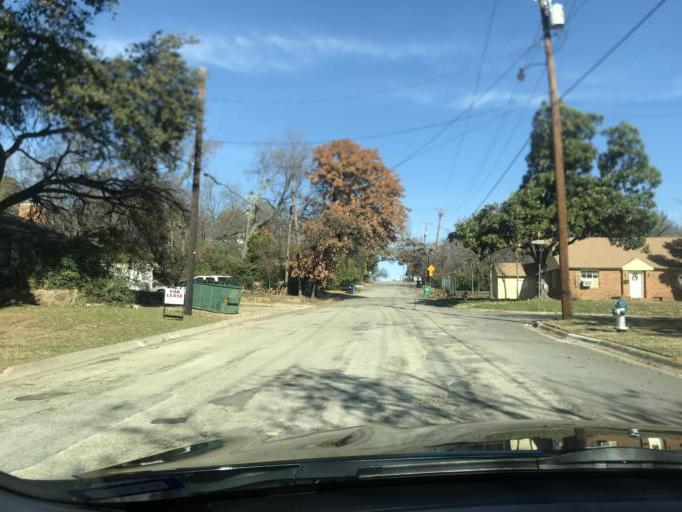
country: US
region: Texas
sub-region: Denton County
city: Denton
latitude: 33.2175
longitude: -97.1588
